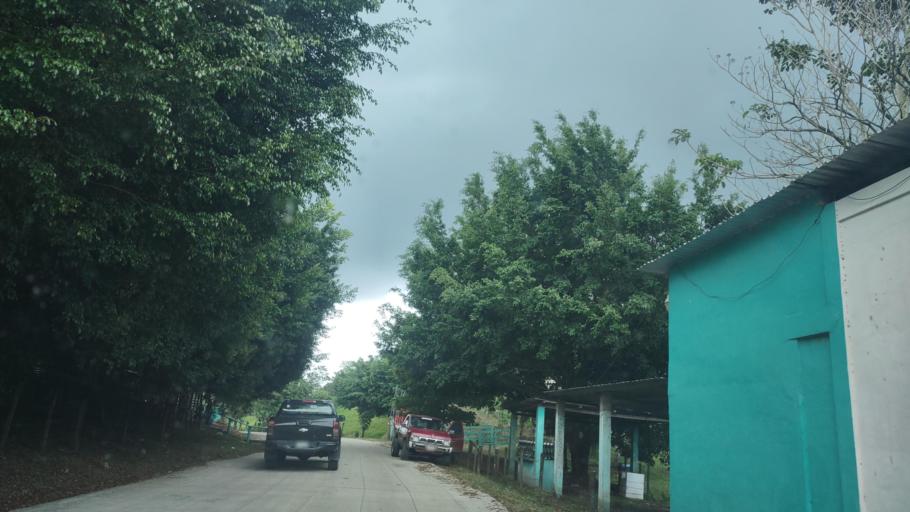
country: MX
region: Veracruz
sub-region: Uxpanapa
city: Poblado 10
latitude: 17.4945
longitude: -94.1703
